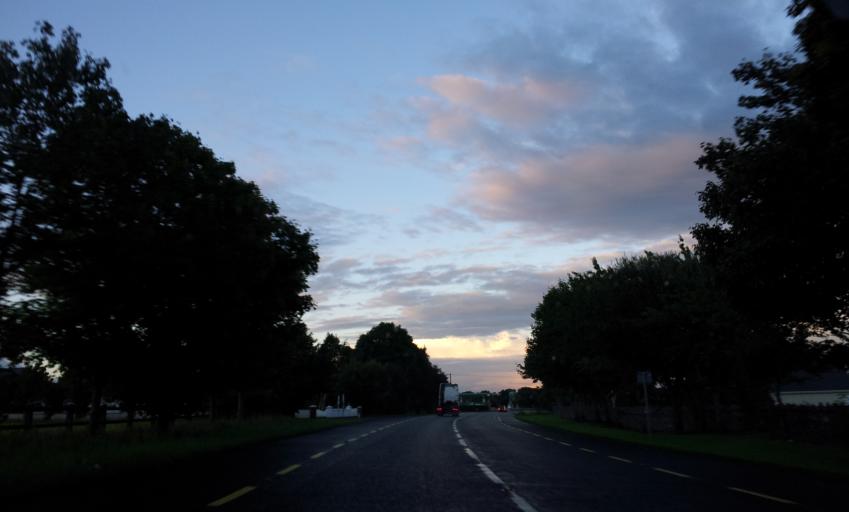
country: IE
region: Munster
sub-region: County Limerick
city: Adare
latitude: 52.5415
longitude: -8.8578
